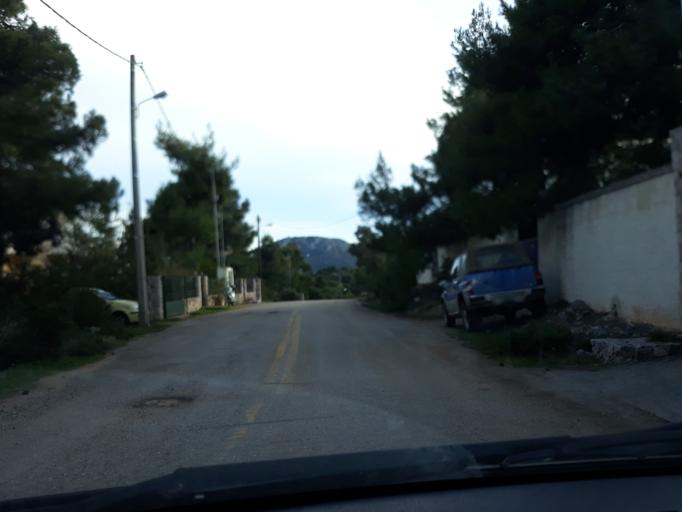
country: GR
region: Attica
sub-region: Nomarchia Anatolikis Attikis
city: Afidnes
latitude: 38.2148
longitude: 23.7975
